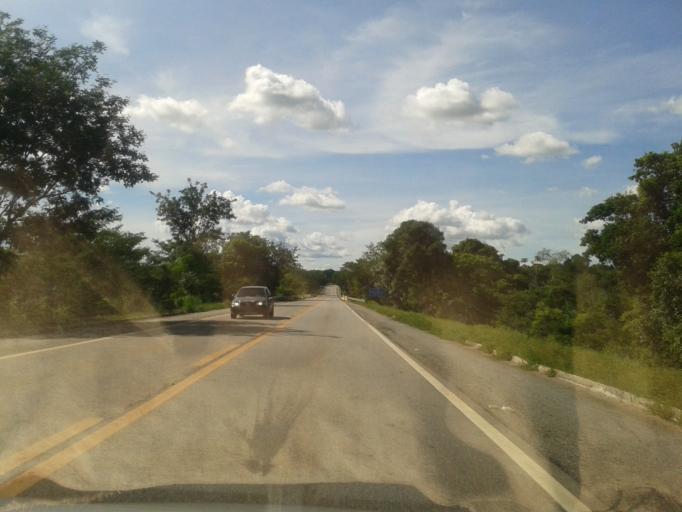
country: BR
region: Goias
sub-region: Mozarlandia
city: Mozarlandia
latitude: -15.1398
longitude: -50.5892
